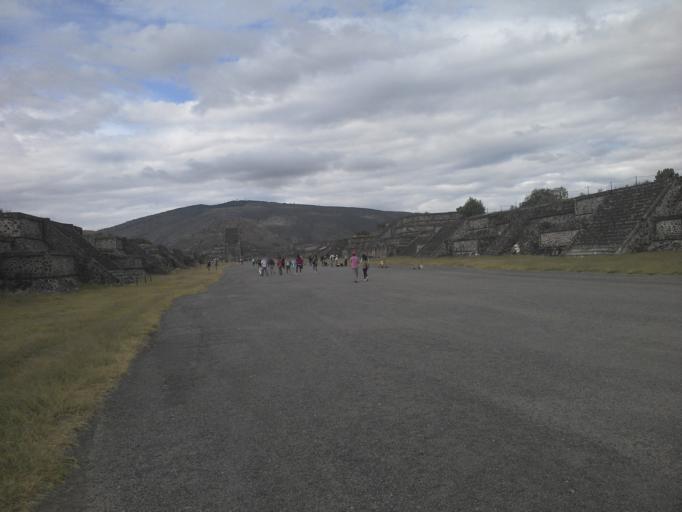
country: MX
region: Morelos
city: San Martin de las Piramides
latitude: 19.6940
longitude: -98.8457
